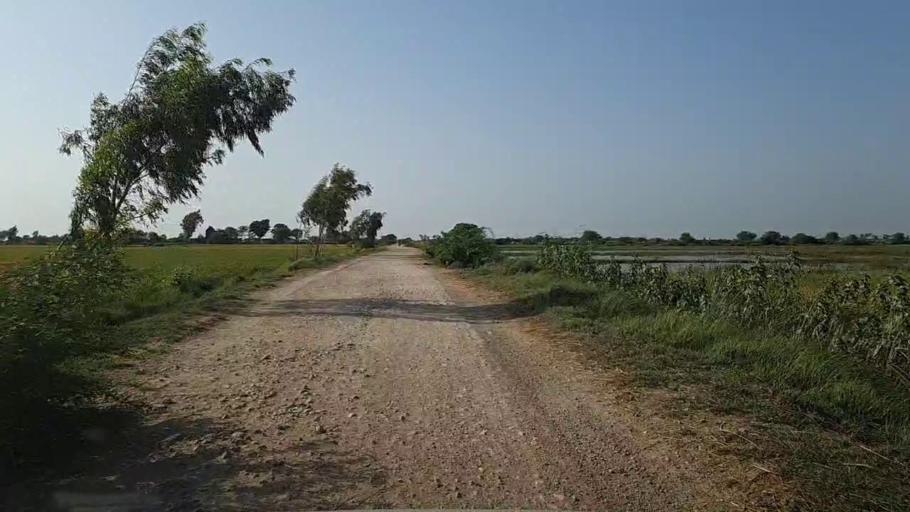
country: PK
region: Sindh
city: Kario
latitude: 24.8051
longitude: 68.5118
